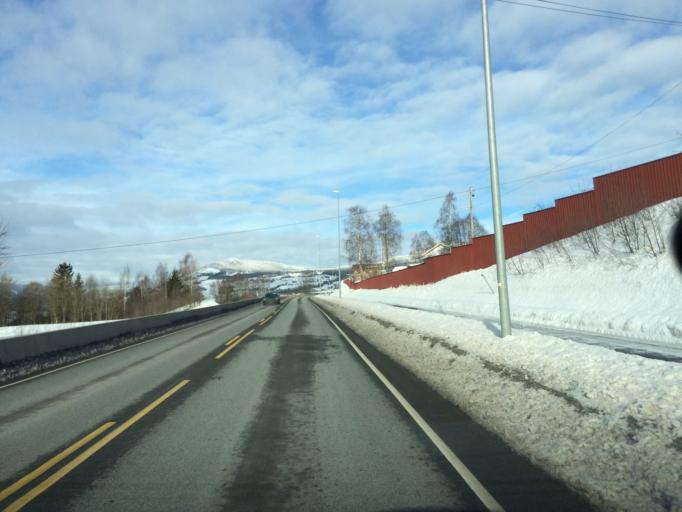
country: NO
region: Oppland
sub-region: Gausdal
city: Segalstad bru
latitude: 61.1952
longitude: 10.3115
